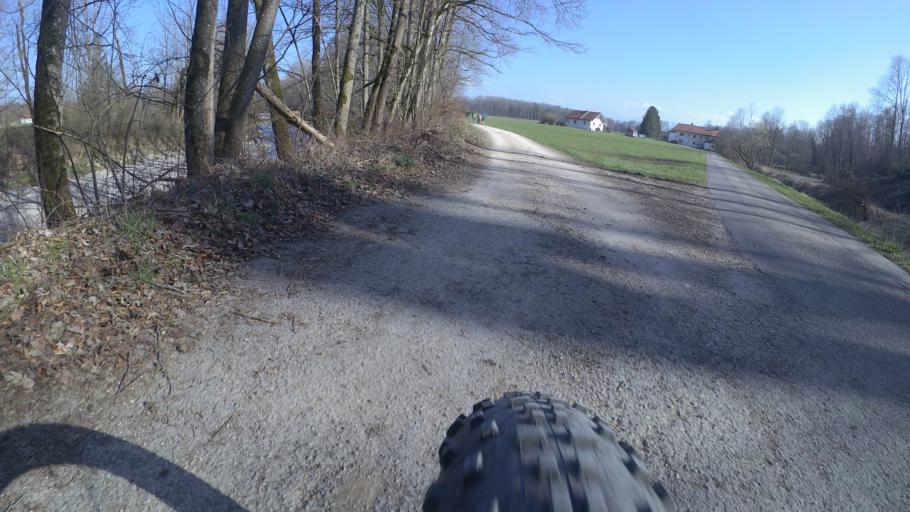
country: DE
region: Bavaria
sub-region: Upper Bavaria
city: Nussdorf
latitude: 47.9337
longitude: 12.6046
